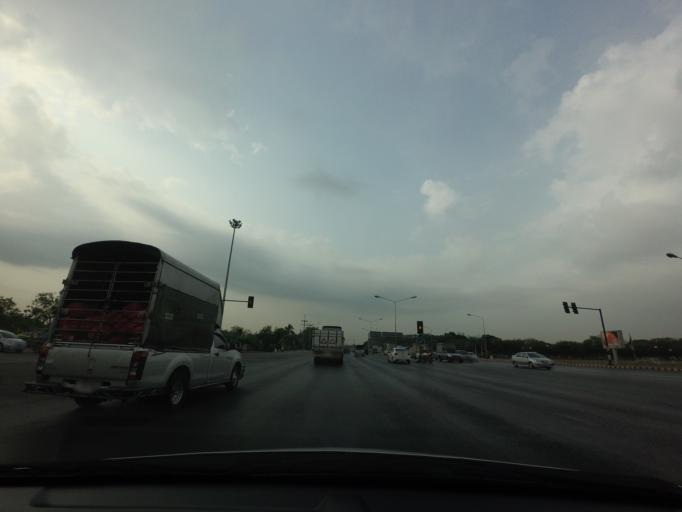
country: TH
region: Bangkok
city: Thawi Watthana
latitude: 13.7771
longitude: 100.3282
